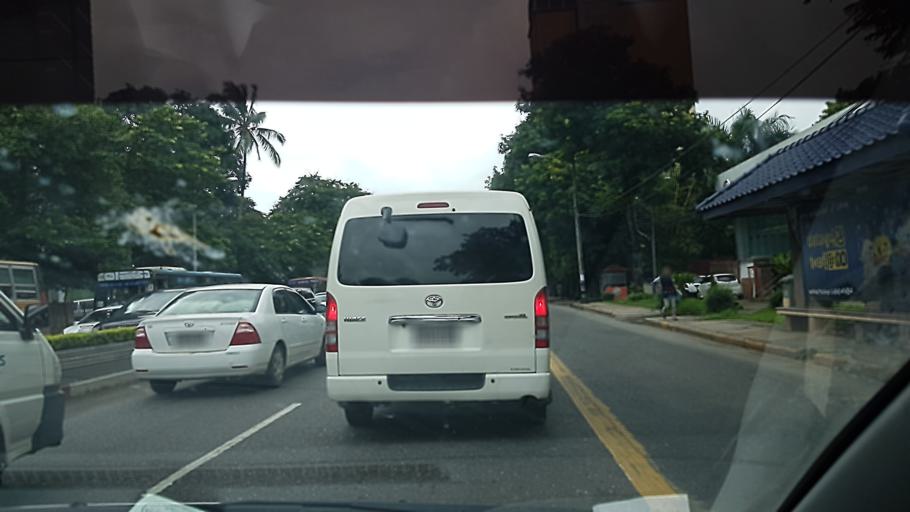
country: MM
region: Yangon
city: Yangon
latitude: 16.8116
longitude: 96.1350
